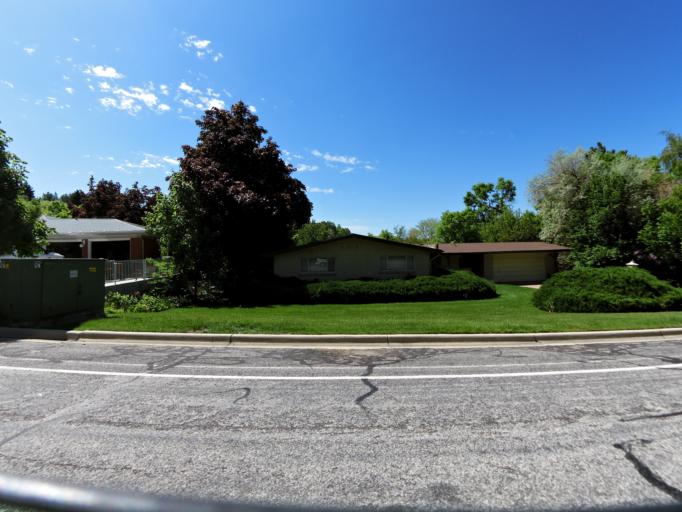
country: US
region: Utah
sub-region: Weber County
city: Uintah
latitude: 41.1682
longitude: -111.9376
